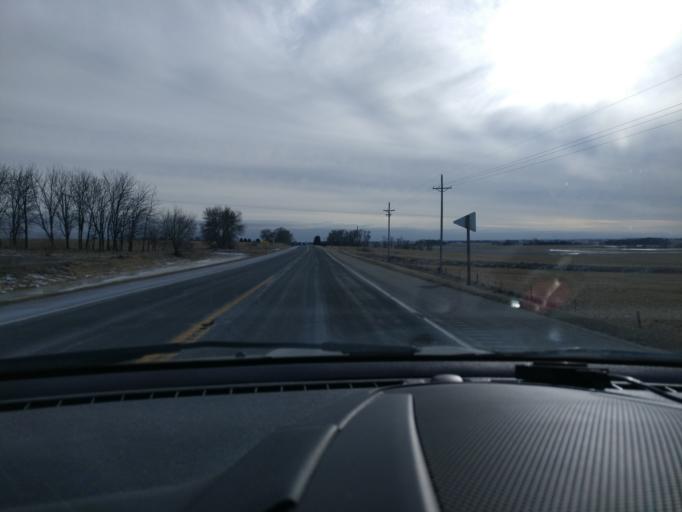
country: US
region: Nebraska
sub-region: Saunders County
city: Yutan
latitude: 41.2793
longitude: -96.5034
